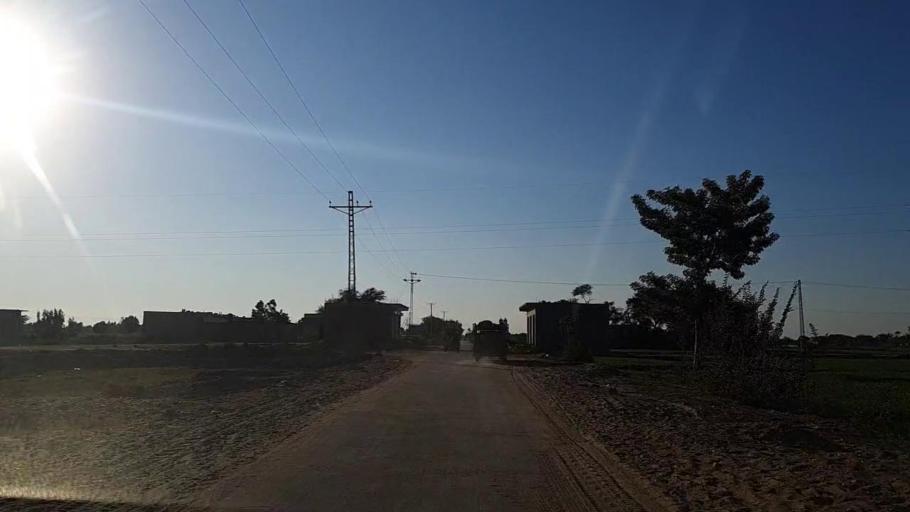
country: PK
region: Sindh
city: Sanghar
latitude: 26.2790
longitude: 68.9294
